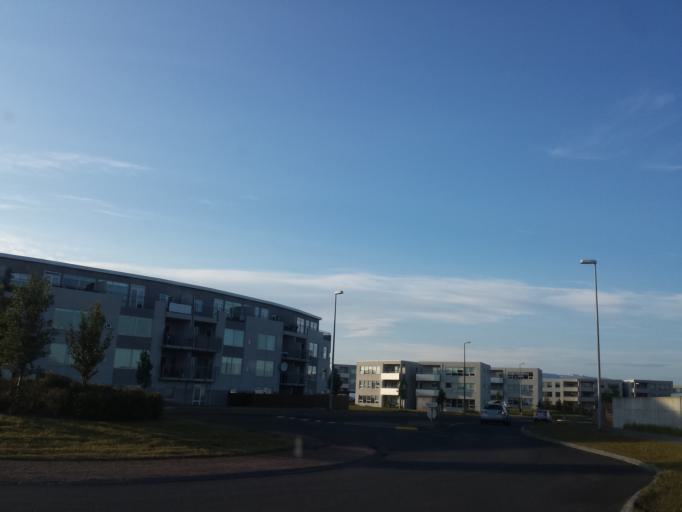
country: IS
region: Capital Region
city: Mosfellsbaer
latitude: 64.0974
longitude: -21.7776
